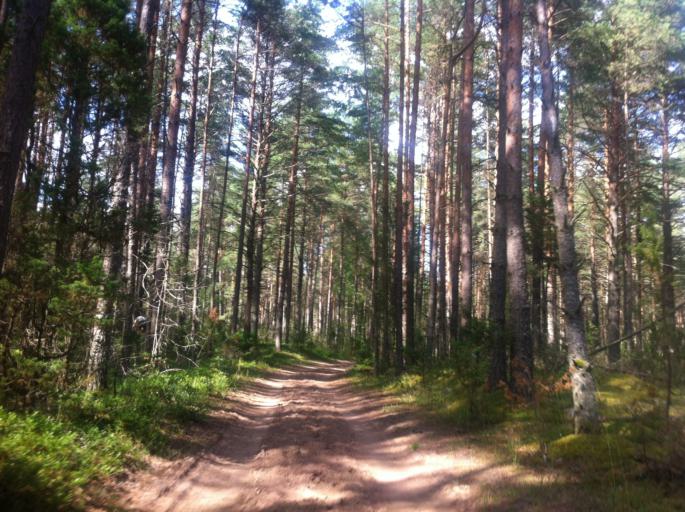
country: RU
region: Pskov
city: Izborsk
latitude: 57.8299
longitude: 27.9377
